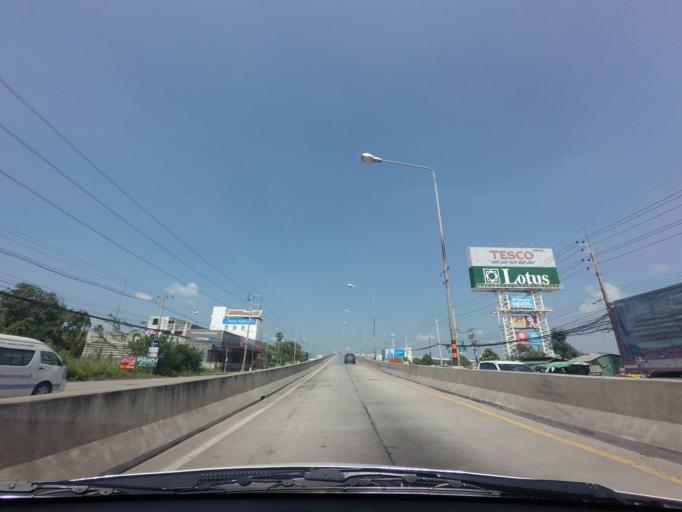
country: TH
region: Nakhon Pathom
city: Nakhon Chai Si
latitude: 13.7914
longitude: 100.1705
